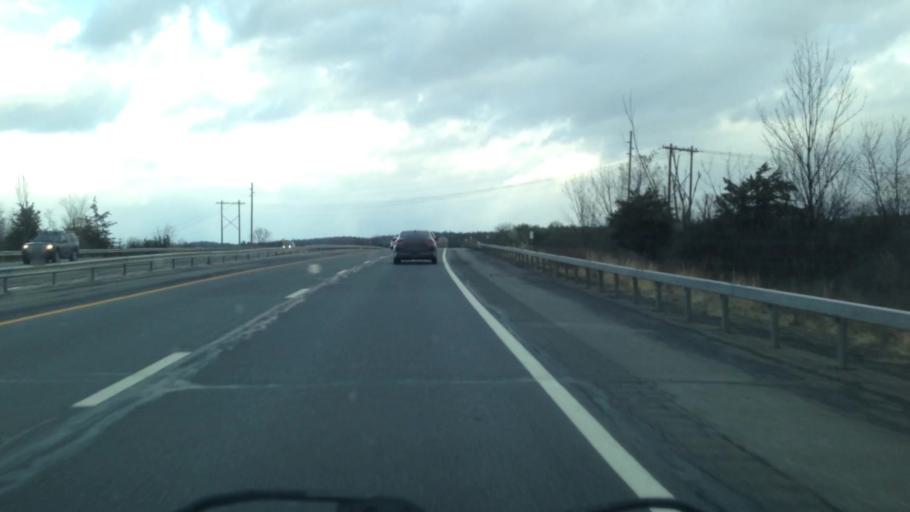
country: US
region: New York
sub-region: Greene County
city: Coxsackie
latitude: 42.4047
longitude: -73.8197
